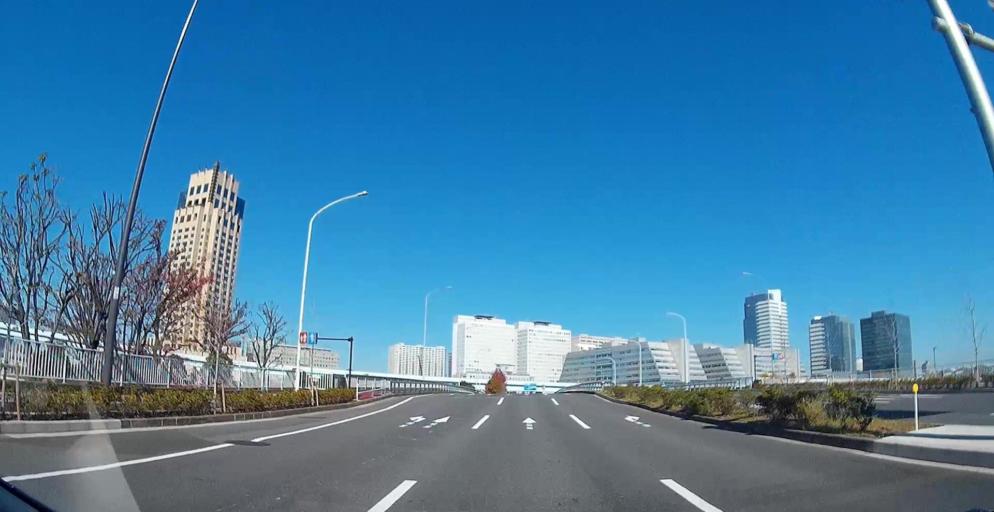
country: JP
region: Tokyo
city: Urayasu
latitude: 35.6268
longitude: 139.7893
